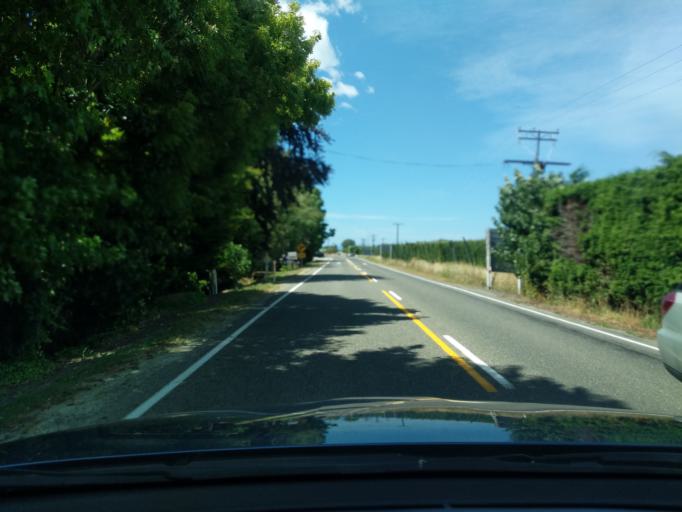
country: NZ
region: Tasman
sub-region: Tasman District
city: Motueka
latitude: -41.0629
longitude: 172.9820
